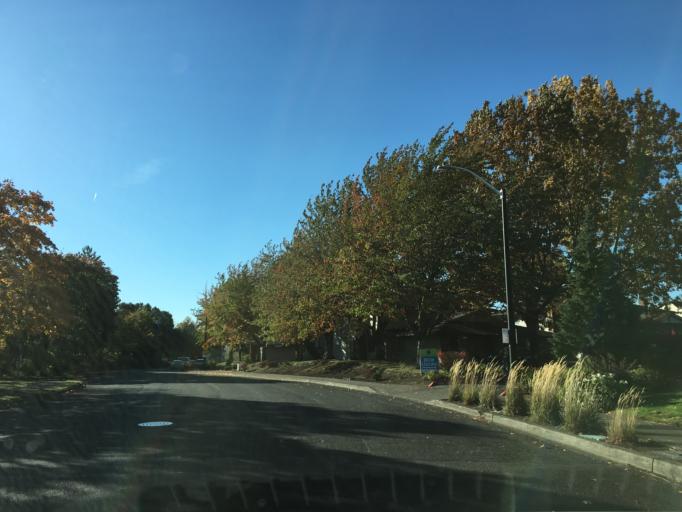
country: US
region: Oregon
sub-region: Multnomah County
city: Wood Village
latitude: 45.5175
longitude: -122.4095
